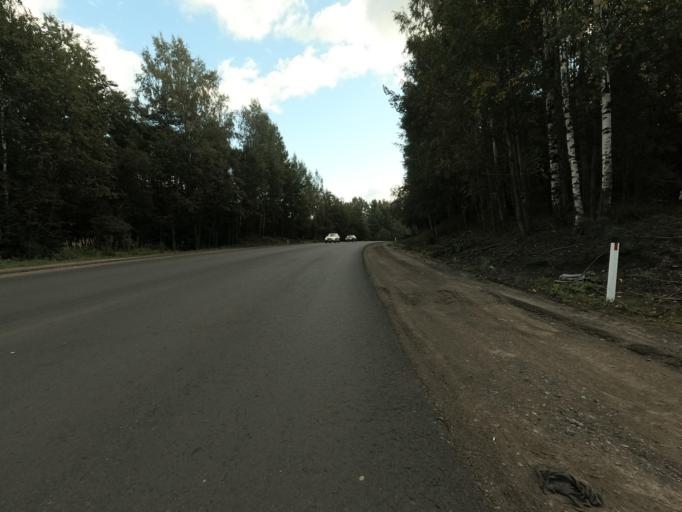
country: RU
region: Leningrad
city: Koltushi
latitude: 59.9667
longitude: 30.6580
